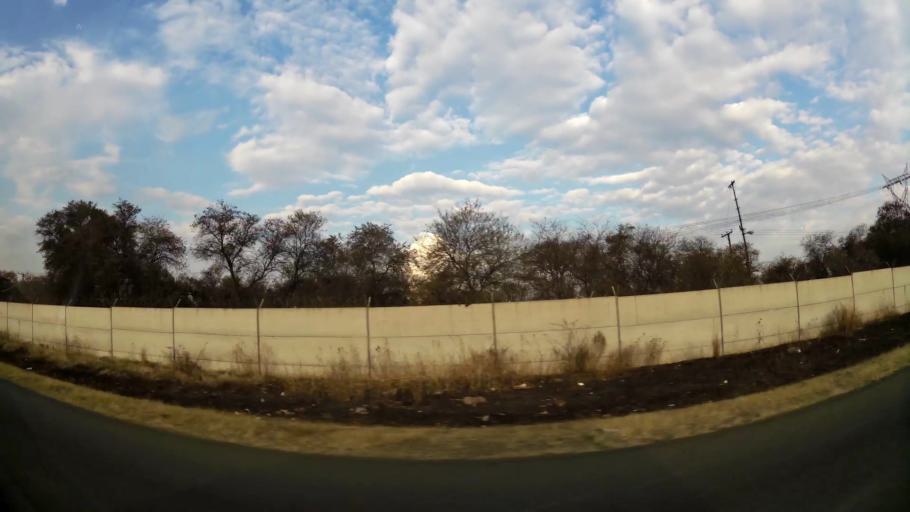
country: ZA
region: Gauteng
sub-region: Sedibeng District Municipality
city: Vanderbijlpark
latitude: -26.6621
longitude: 27.7985
